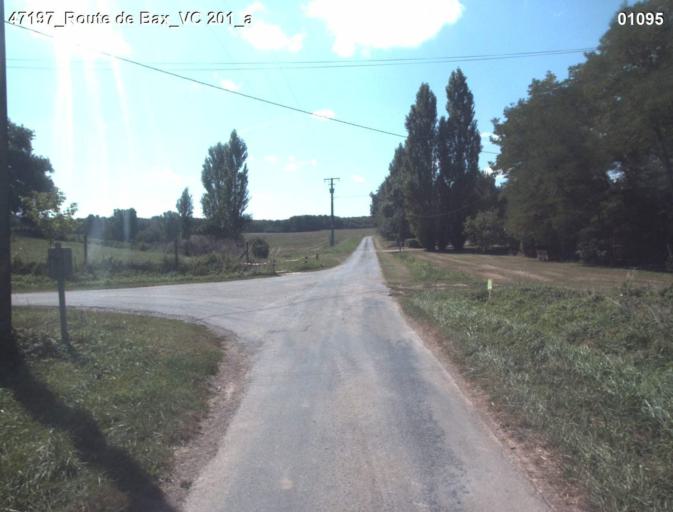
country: FR
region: Aquitaine
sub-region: Departement du Lot-et-Garonne
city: Laplume
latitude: 44.0722
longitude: 0.4866
